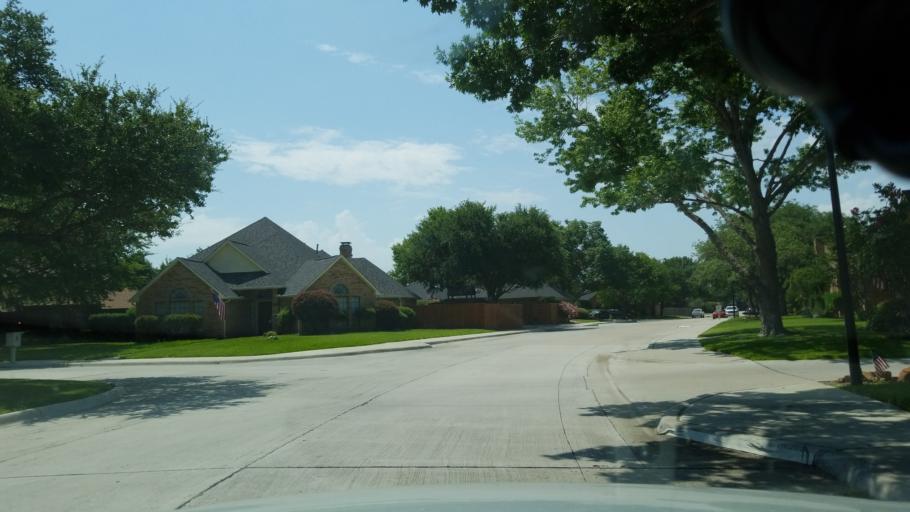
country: US
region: Texas
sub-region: Dallas County
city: Coppell
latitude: 32.9687
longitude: -96.9806
